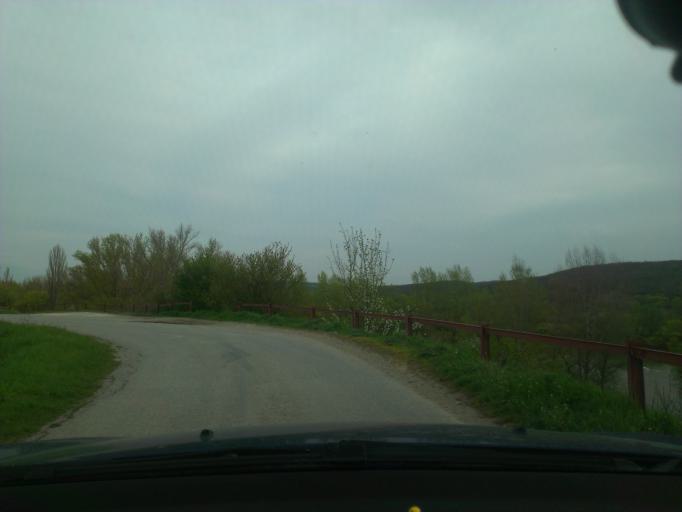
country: SK
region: Trnavsky
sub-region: Okres Trnava
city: Piestany
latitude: 48.5164
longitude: 17.8150
